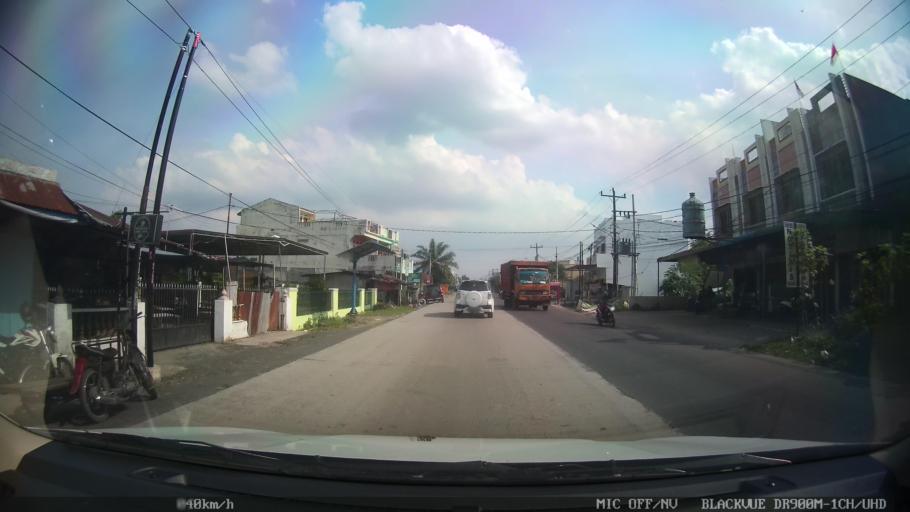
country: ID
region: North Sumatra
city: Binjai
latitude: 3.6230
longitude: 98.4957
